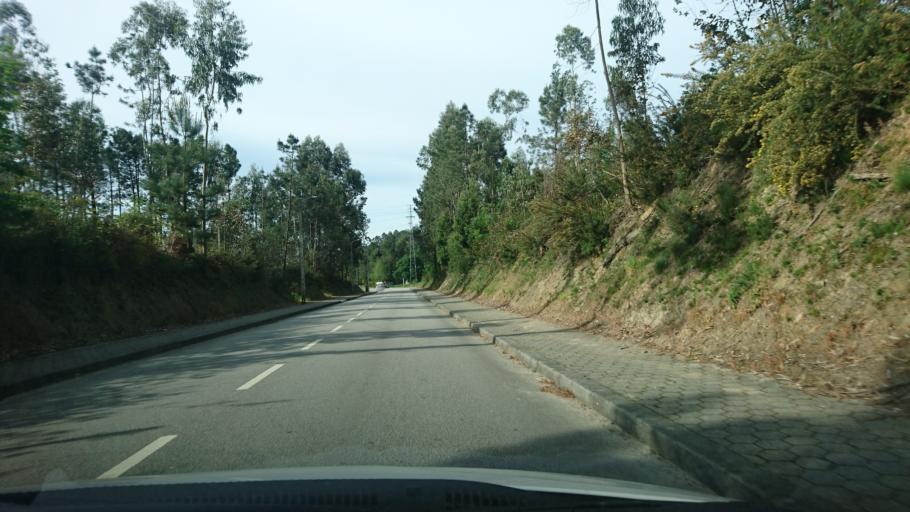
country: PT
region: Aveiro
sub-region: Oliveira de Azemeis
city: Sao Roque
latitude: 40.8759
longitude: -8.4753
